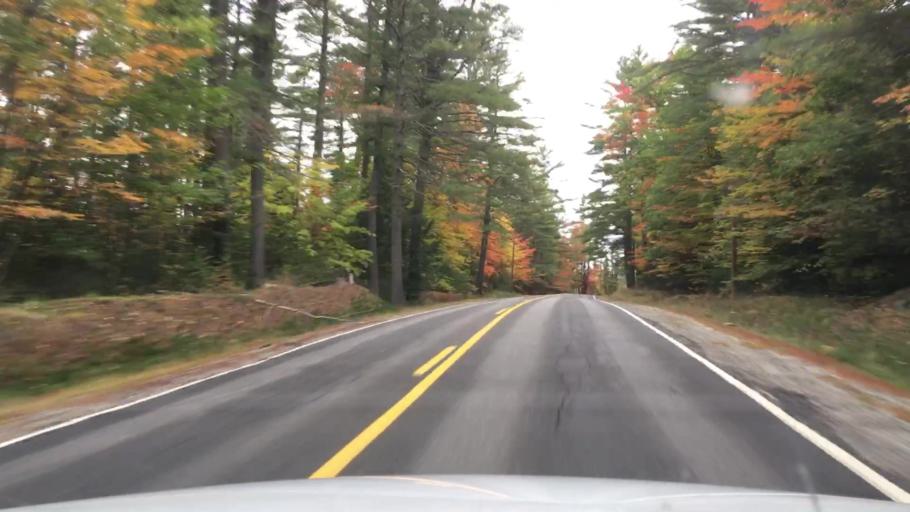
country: US
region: Maine
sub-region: Oxford County
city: Bethel
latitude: 44.3872
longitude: -70.7979
